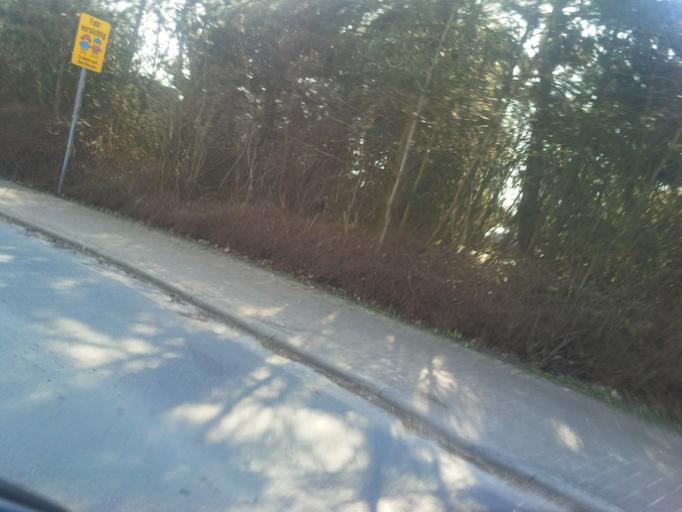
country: DE
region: Mecklenburg-Vorpommern
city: Lambrechtshagen
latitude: 54.1154
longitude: 12.0347
